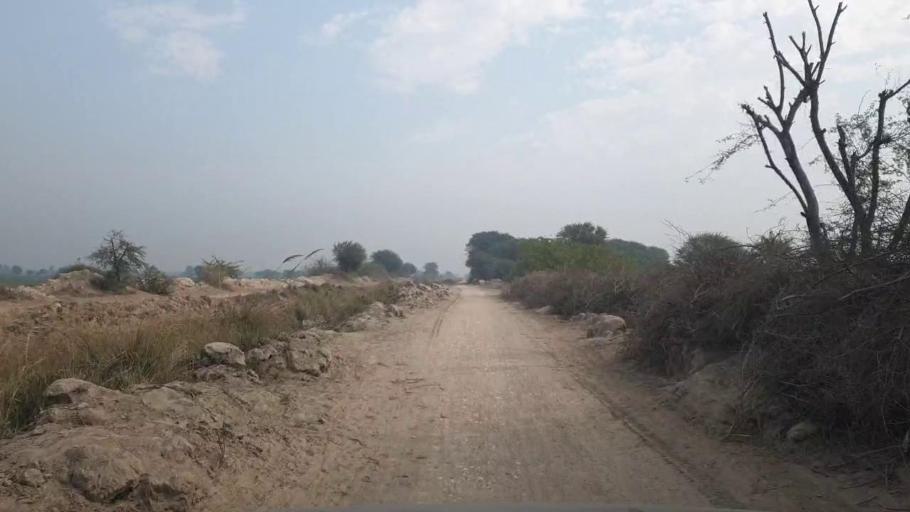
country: PK
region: Sindh
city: Hala
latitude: 25.7651
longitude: 68.4492
